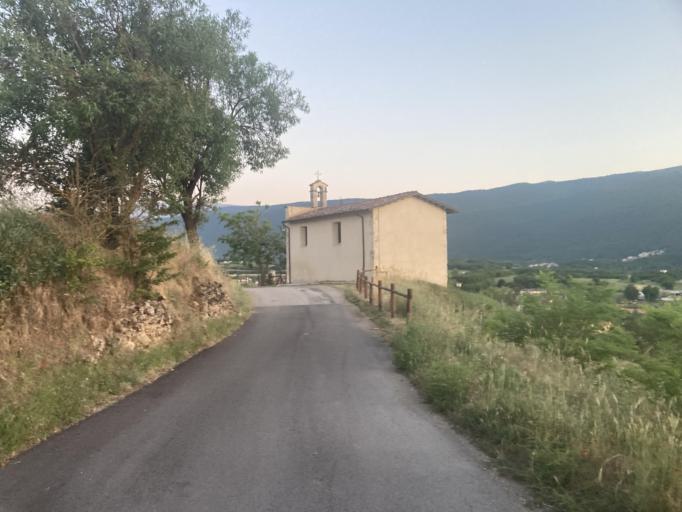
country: IT
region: Abruzzo
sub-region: Provincia dell' Aquila
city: San Demetrio Ne' Vestini
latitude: 42.2934
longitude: 13.5521
